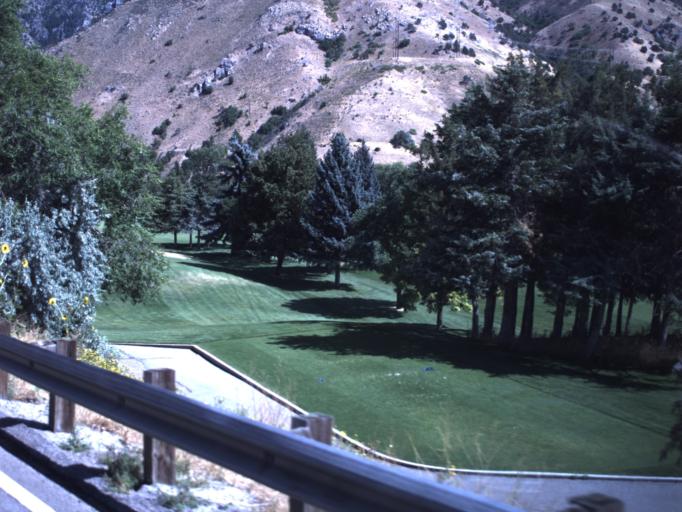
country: US
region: Utah
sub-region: Cache County
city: North Logan
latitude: 41.7439
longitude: -111.7951
